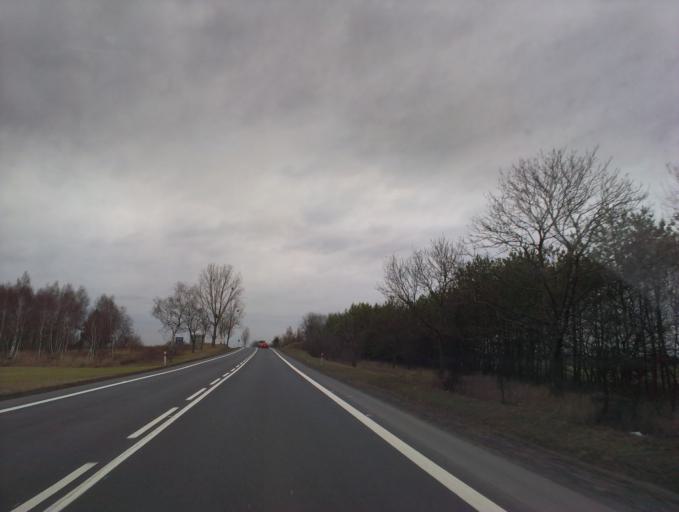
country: PL
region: Greater Poland Voivodeship
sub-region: Powiat poznanski
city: Zlotniki
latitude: 52.5419
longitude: 16.8387
